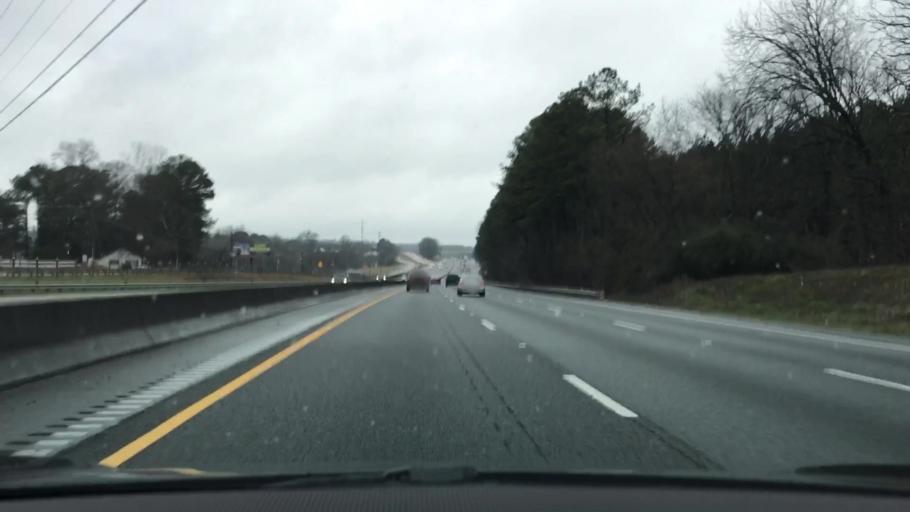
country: US
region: Georgia
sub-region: Newton County
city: Porterdale
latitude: 33.6140
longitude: -83.9105
